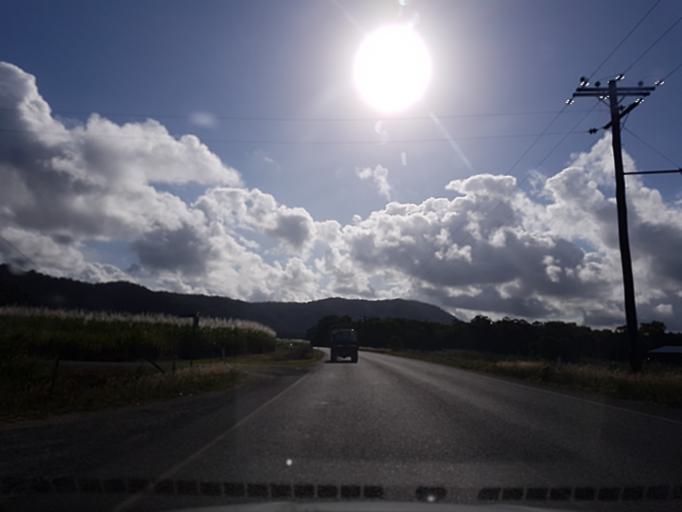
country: AU
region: Queensland
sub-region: Cairns
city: Port Douglas
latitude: -16.3132
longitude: 145.4004
